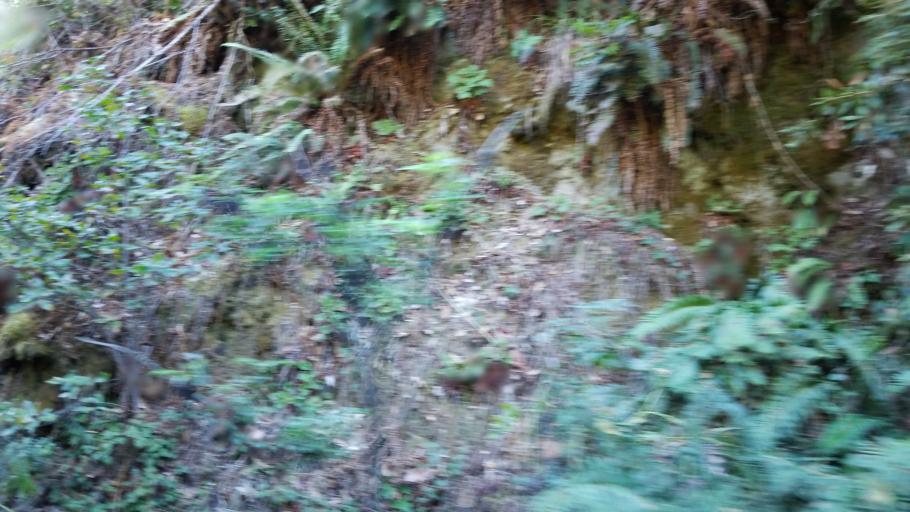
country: US
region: California
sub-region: Mendocino County
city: Fort Bragg
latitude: 39.4468
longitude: -123.7885
